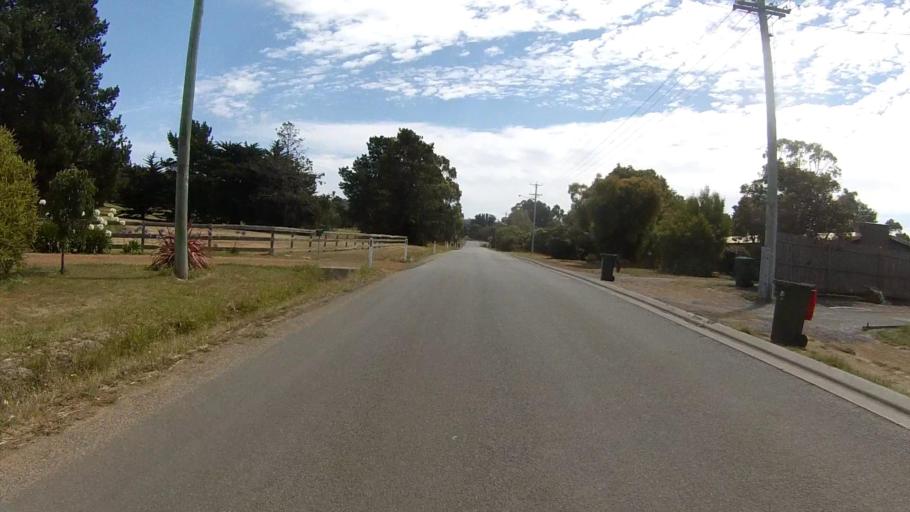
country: AU
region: Tasmania
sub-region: Clarence
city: Sandford
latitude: -42.9885
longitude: 147.5202
